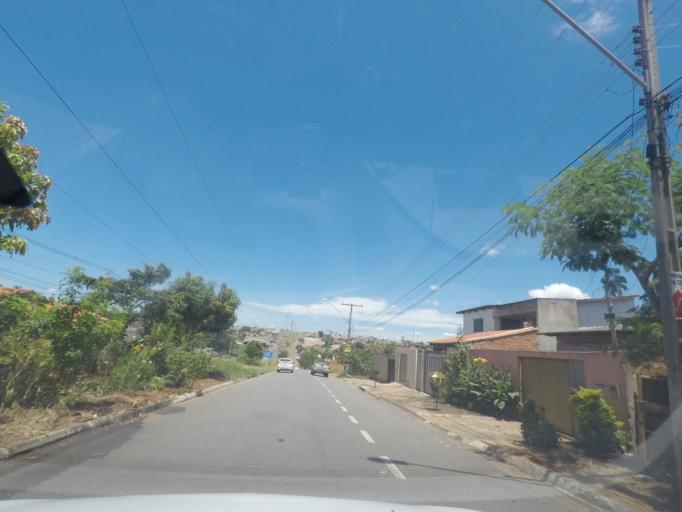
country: BR
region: Goias
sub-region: Goiania
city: Goiania
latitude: -16.7318
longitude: -49.3536
